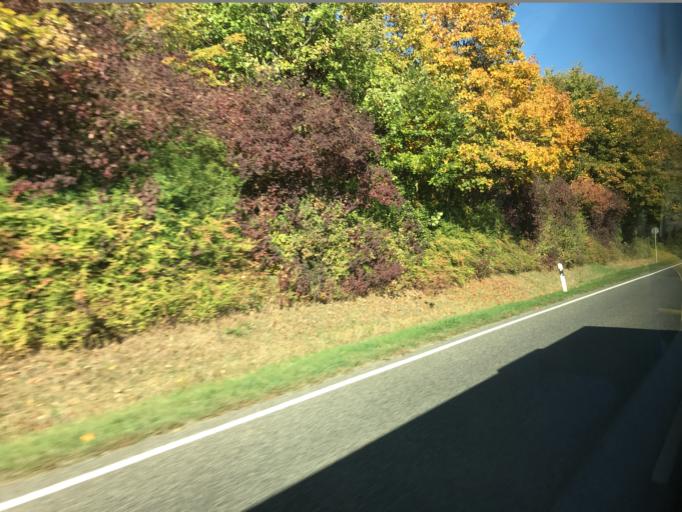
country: DE
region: Hesse
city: Kelkheim (Taunus)
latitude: 50.1479
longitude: 8.4596
